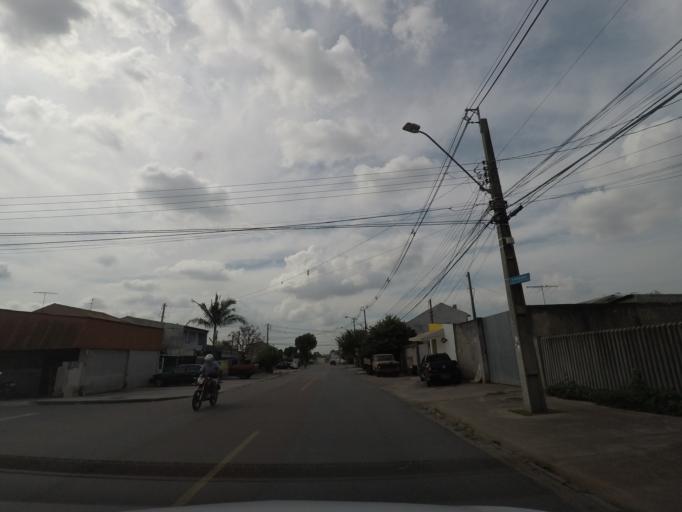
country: BR
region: Parana
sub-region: Pinhais
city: Pinhais
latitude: -25.4756
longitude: -49.1971
